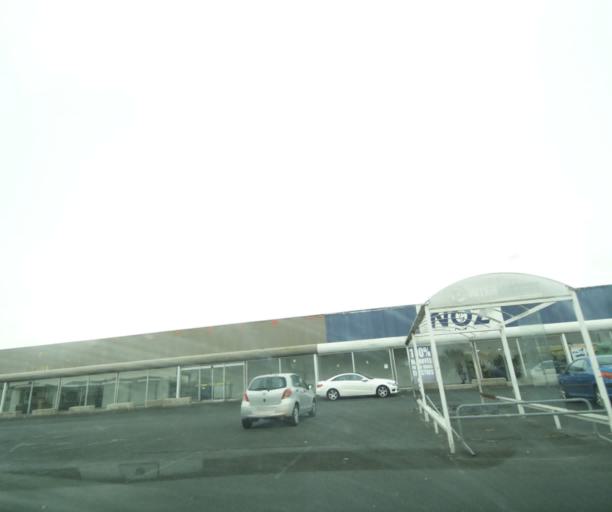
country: FR
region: Poitou-Charentes
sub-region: Departement de la Charente-Maritime
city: Breuil-Magne
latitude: 45.9516
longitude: -0.9364
